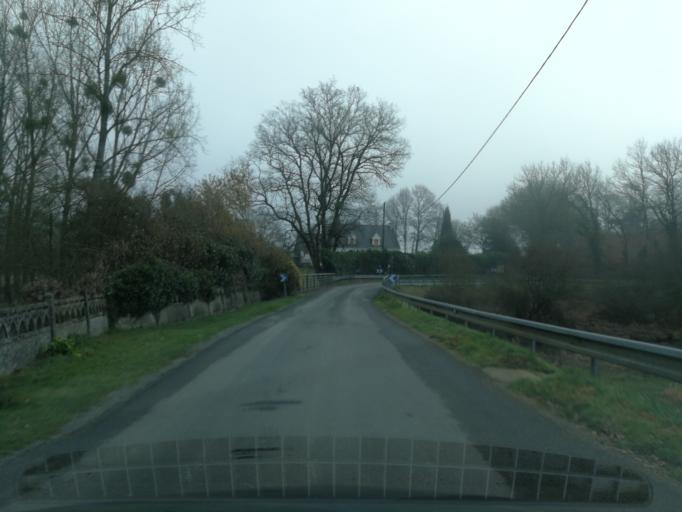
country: FR
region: Brittany
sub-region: Departement du Morbihan
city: La Vraie-Croix
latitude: 47.7324
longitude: -2.5064
